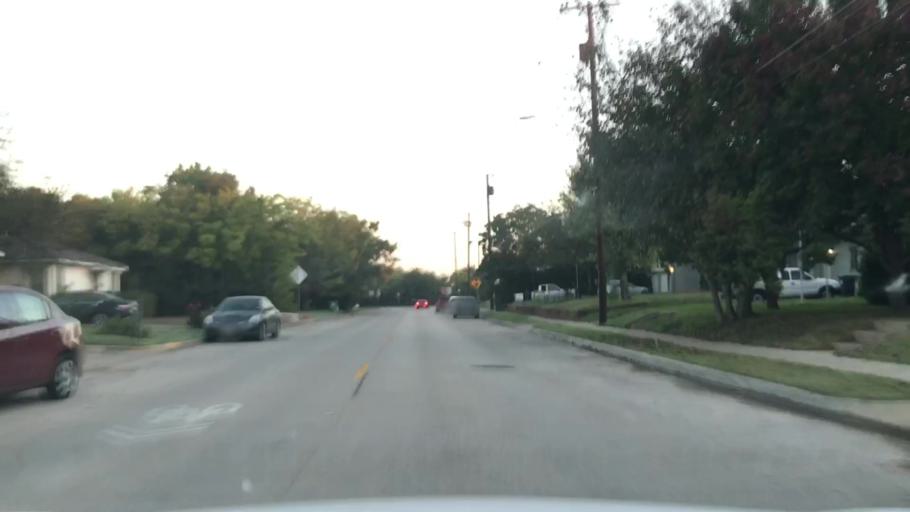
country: US
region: Texas
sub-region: Denton County
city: Denton
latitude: 33.2172
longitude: -97.1506
